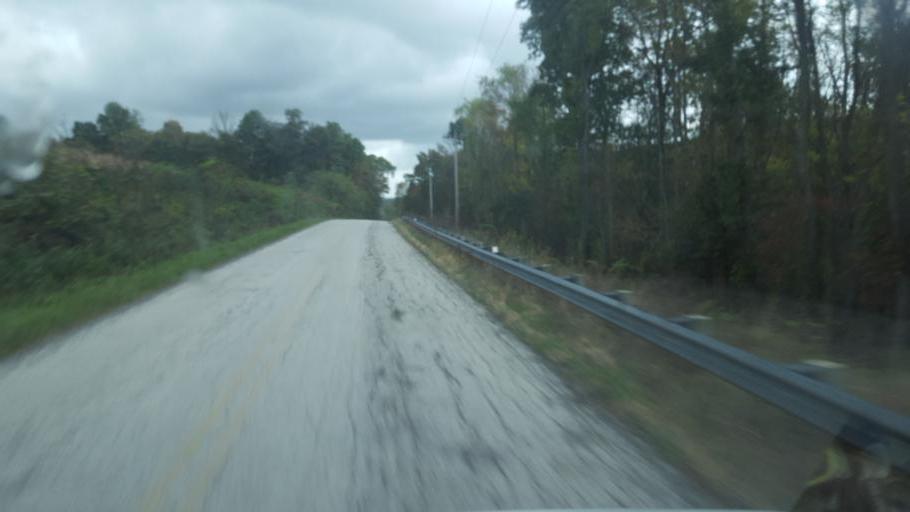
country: US
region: Ohio
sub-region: Ashland County
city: Loudonville
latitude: 40.5730
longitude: -82.1657
